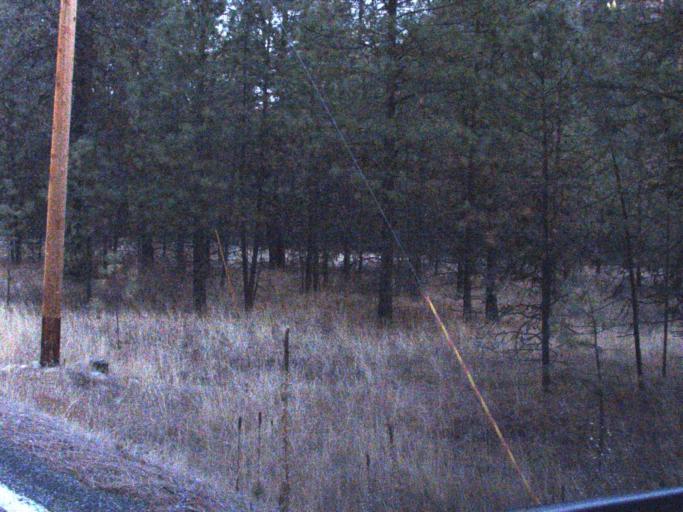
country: US
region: Washington
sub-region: Ferry County
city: Republic
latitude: 48.4033
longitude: -118.7323
